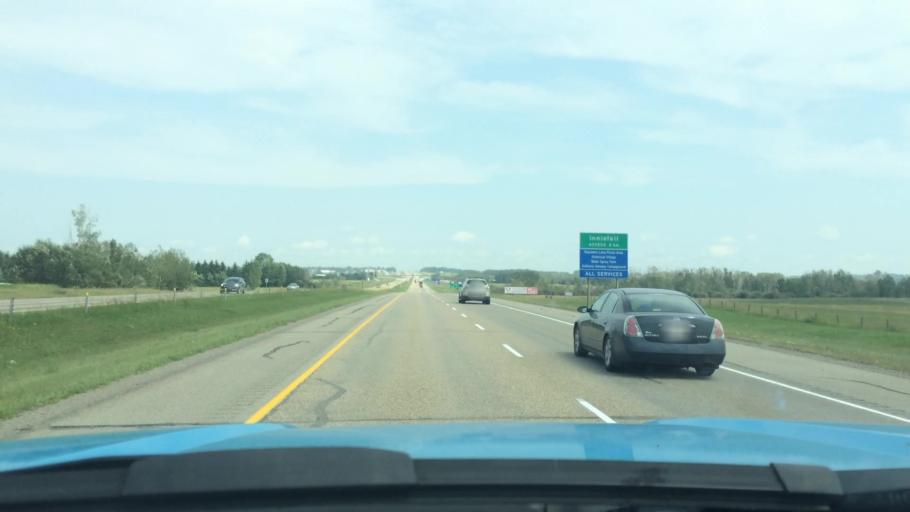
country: CA
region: Alberta
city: Penhold
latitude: 51.9868
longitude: -113.9847
